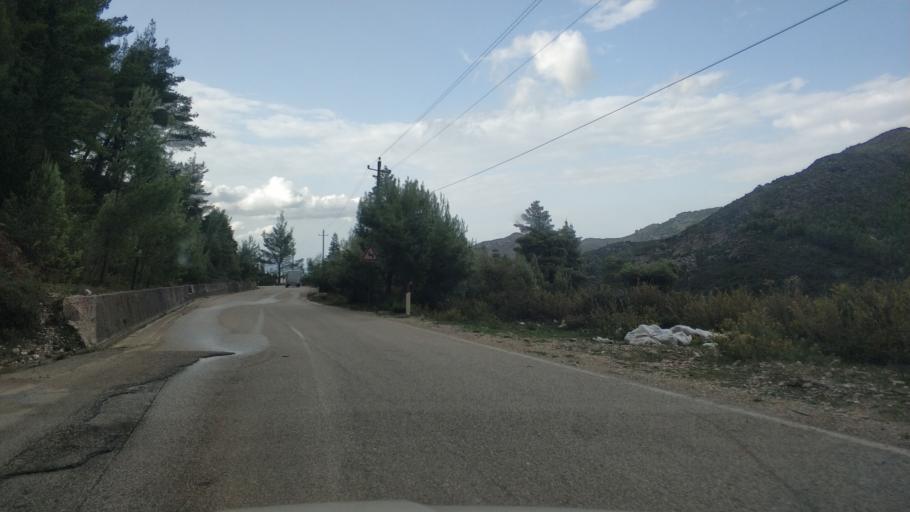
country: AL
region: Vlore
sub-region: Rrethi i Vlores
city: Orikum
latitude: 40.2584
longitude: 19.5269
